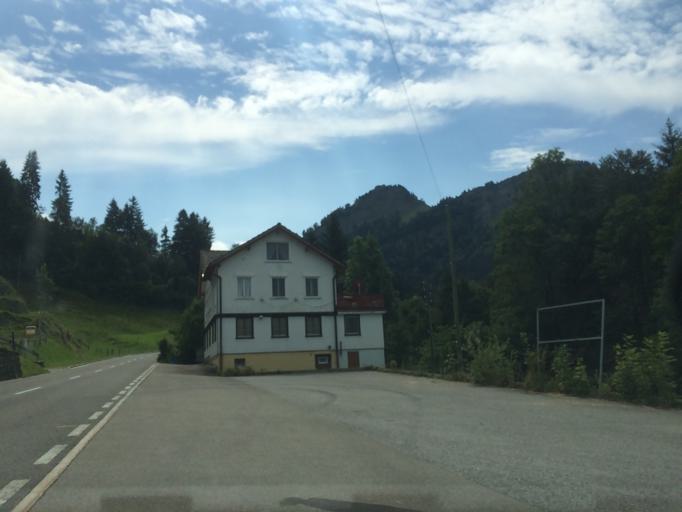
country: CH
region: Appenzell Ausserrhoden
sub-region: Bezirk Hinterland
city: Urnasch
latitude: 47.2861
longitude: 9.2797
